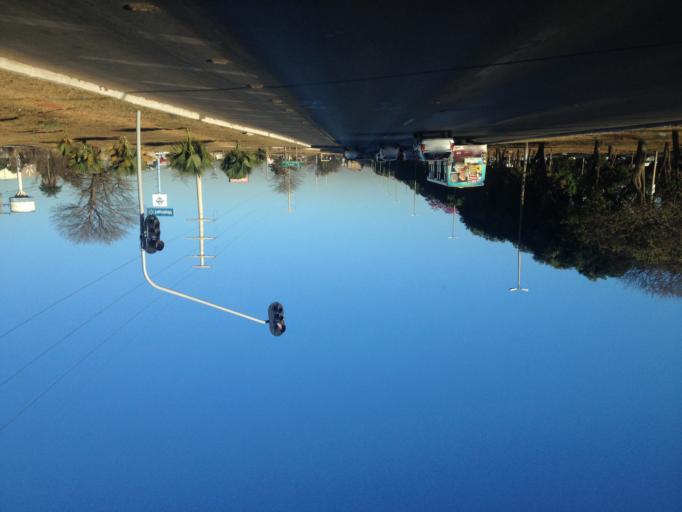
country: BR
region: Federal District
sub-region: Brasilia
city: Brasilia
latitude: -15.7874
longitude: -47.9421
